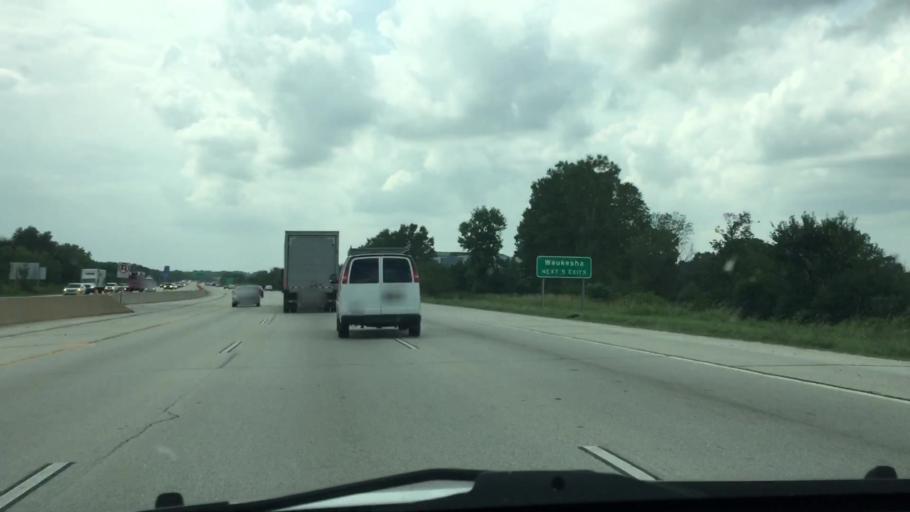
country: US
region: Wisconsin
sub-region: Waukesha County
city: Brookfield
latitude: 43.0291
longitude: -88.1308
